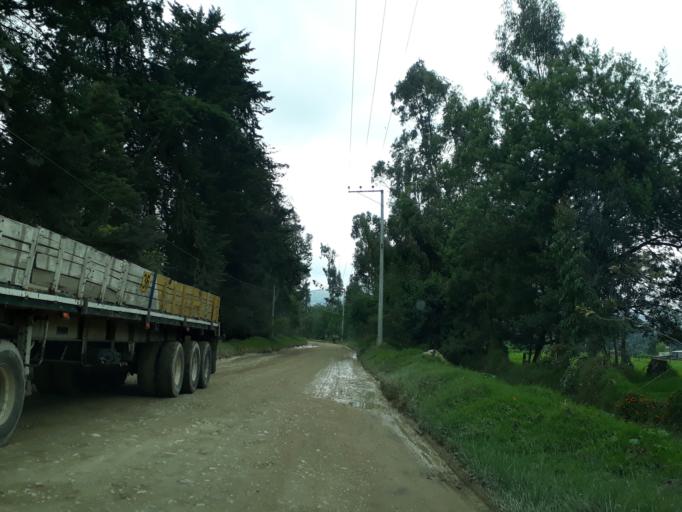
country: CO
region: Cundinamarca
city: Sesquile
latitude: 5.0630
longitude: -73.8040
